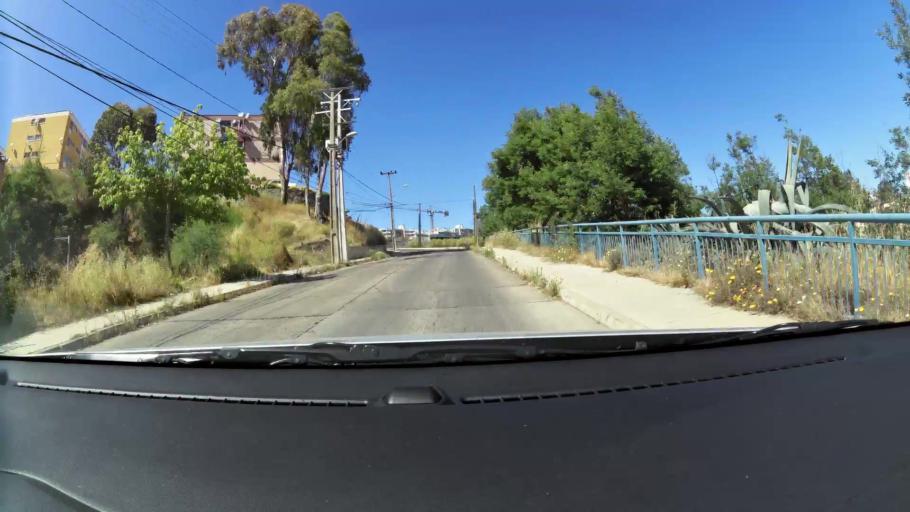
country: CL
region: Valparaiso
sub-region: Provincia de Valparaiso
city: Vina del Mar
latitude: -33.0574
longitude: -71.5834
